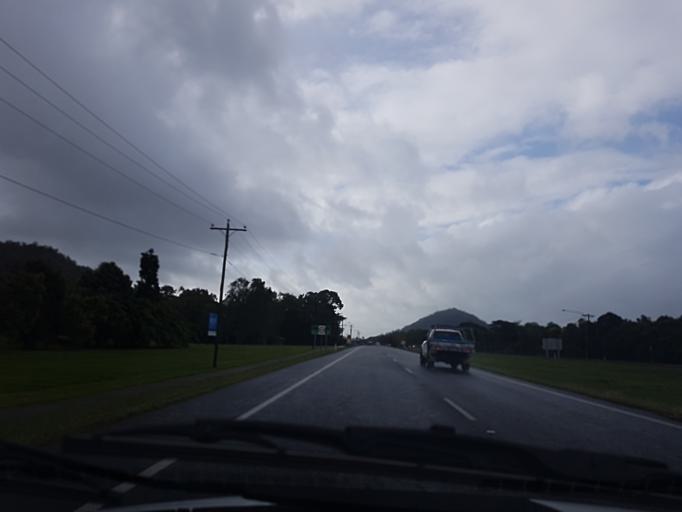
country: AU
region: Queensland
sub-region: Cairns
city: Trinity Beach
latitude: -16.8199
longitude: 145.6928
